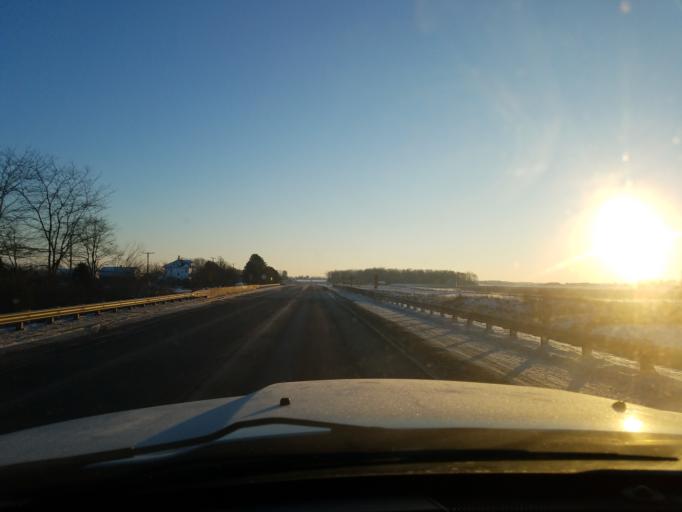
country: US
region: Indiana
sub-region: Marshall County
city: Bremen
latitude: 41.4497
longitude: -86.2145
